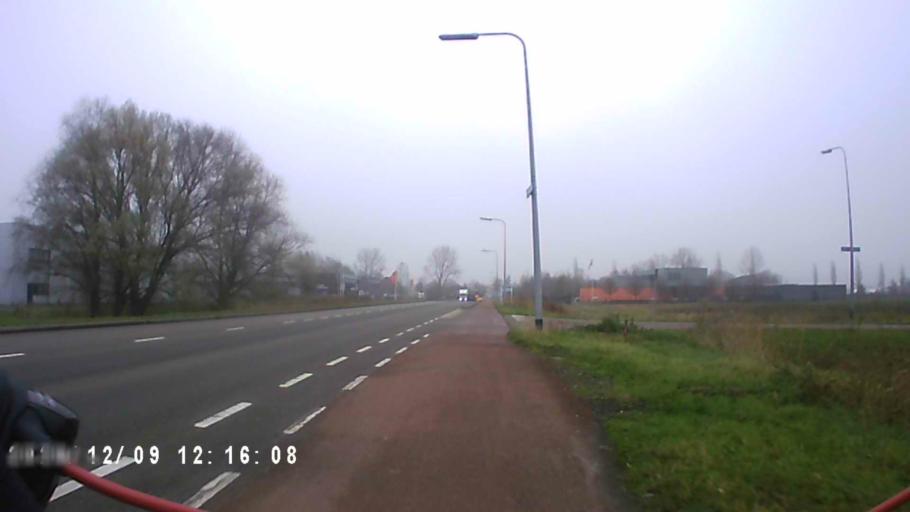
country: NL
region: Groningen
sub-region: Gemeente Groningen
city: Oosterpark
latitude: 53.2070
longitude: 6.6166
